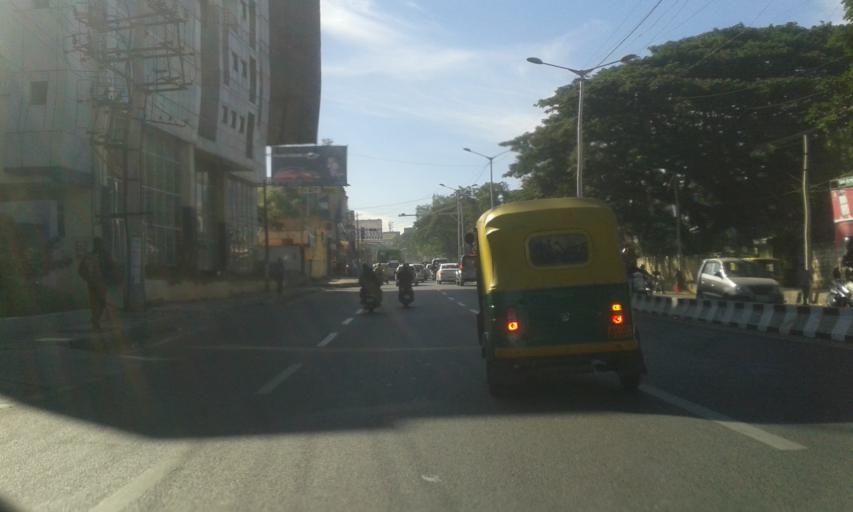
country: IN
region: Karnataka
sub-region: Bangalore Urban
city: Bangalore
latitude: 12.9450
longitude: 77.6074
